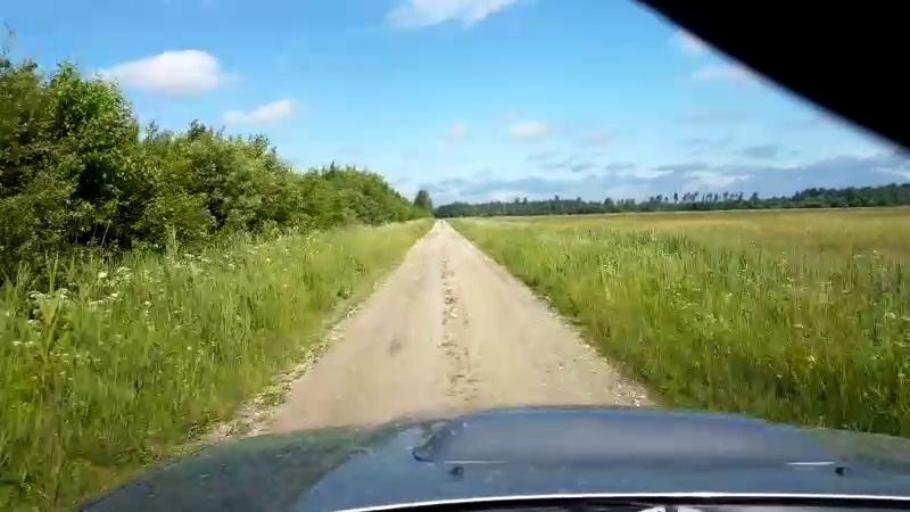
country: EE
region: Paernumaa
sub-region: Sindi linn
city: Sindi
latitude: 58.4930
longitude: 24.6503
